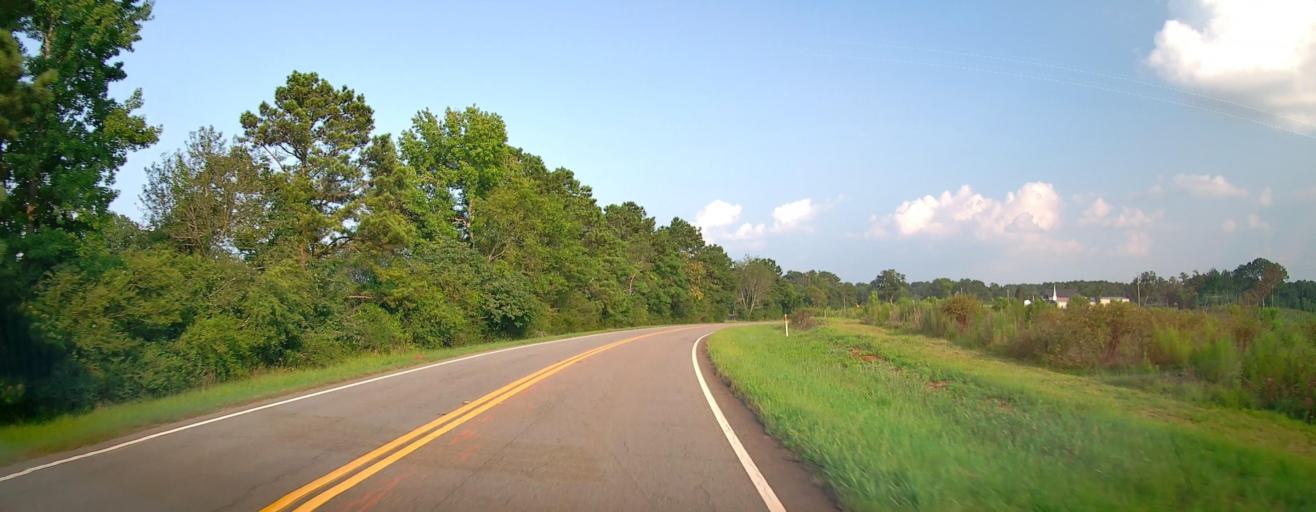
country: US
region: Georgia
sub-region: Jones County
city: Gray
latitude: 33.0585
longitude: -83.5627
